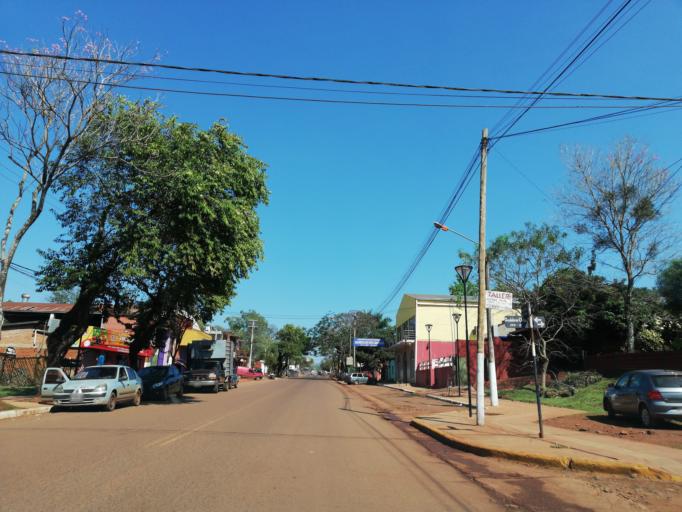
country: AR
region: Misiones
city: Puerto Eldorado
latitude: -26.4069
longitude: -54.6635
